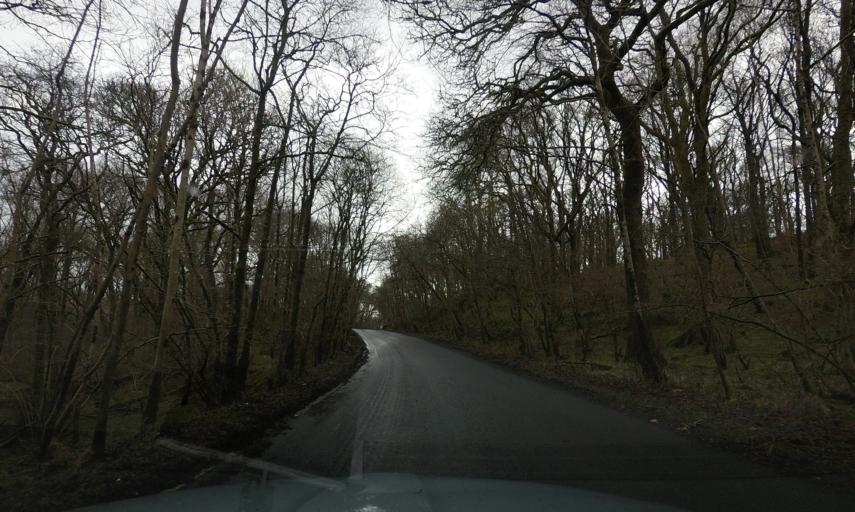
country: GB
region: Scotland
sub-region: West Dunbartonshire
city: Balloch
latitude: 56.0952
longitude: -4.5543
